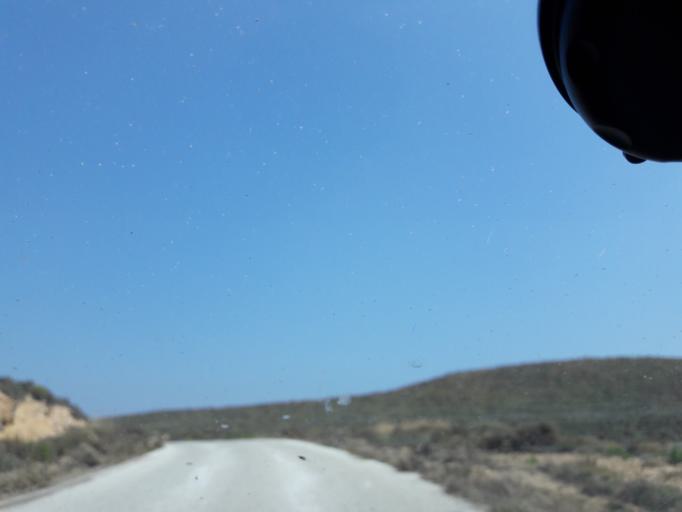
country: GR
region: North Aegean
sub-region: Nomos Lesvou
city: Myrina
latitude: 39.9785
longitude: 25.3453
